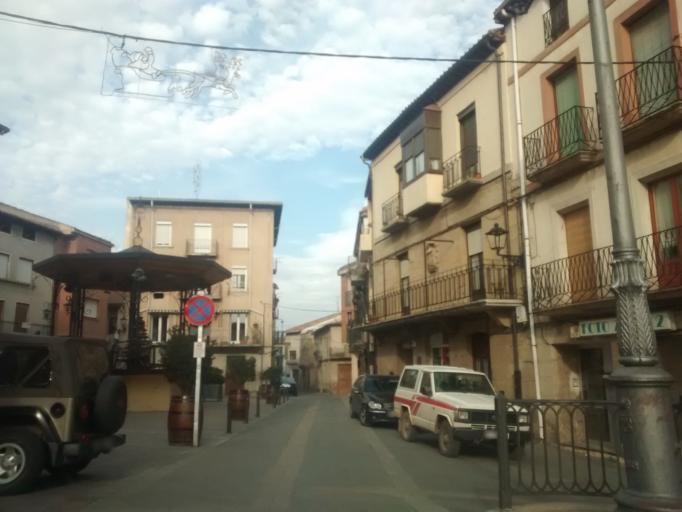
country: ES
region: La Rioja
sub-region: Provincia de La Rioja
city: Cenicero
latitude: 42.4815
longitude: -2.6420
